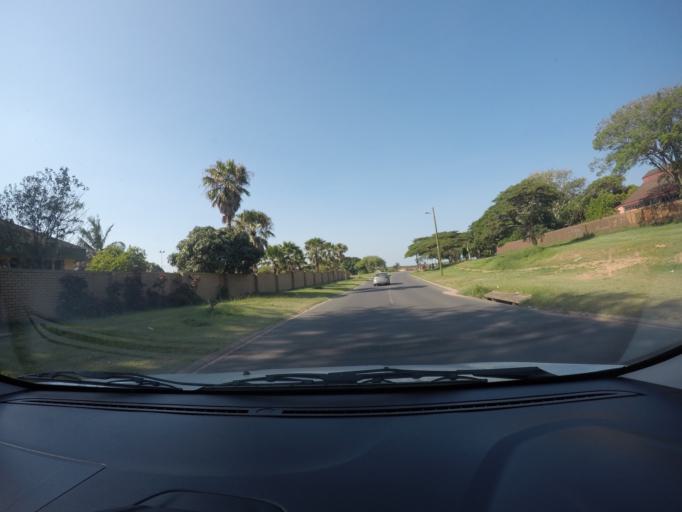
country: ZA
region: KwaZulu-Natal
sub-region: uThungulu District Municipality
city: Richards Bay
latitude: -28.7219
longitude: 32.0411
